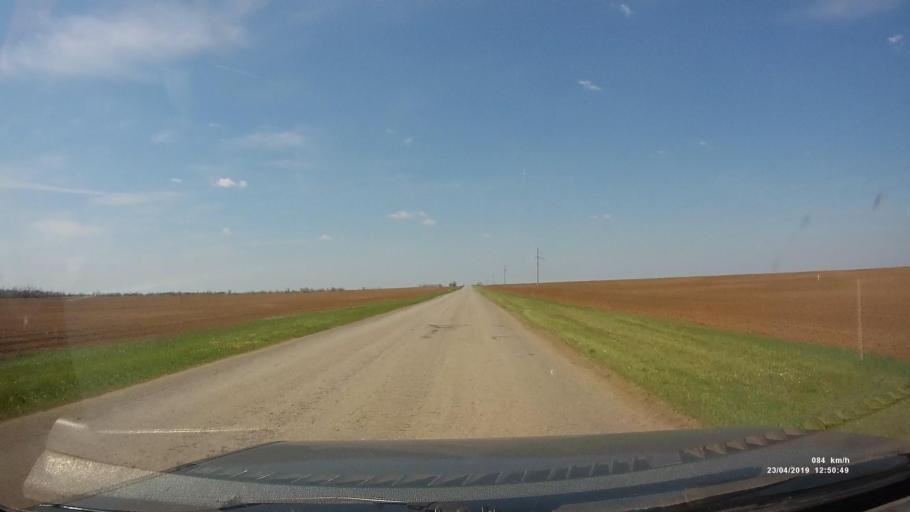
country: RU
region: Kalmykiya
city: Yashalta
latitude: 46.5490
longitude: 42.6309
